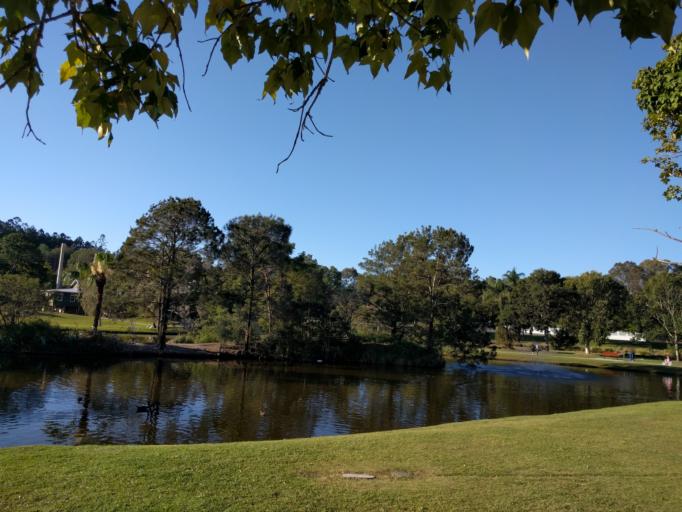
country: AU
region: Queensland
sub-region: Gympie Regional Council
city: Monkland
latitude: -26.2158
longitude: 152.6852
